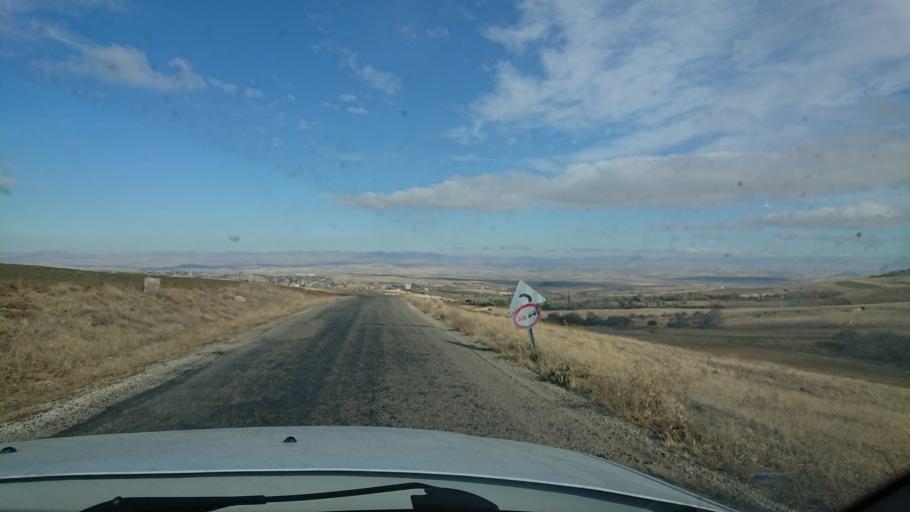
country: TR
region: Aksaray
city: Agacoren
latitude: 38.8421
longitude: 33.9527
